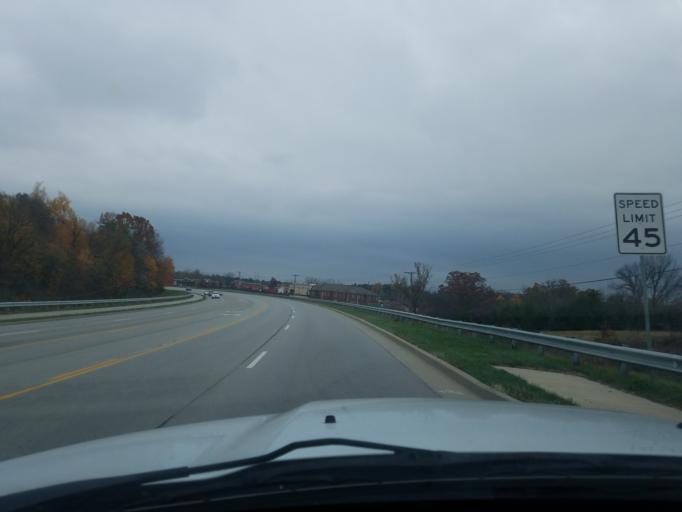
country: US
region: Kentucky
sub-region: Nelson County
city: Bardstown
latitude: 37.8157
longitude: -85.4273
